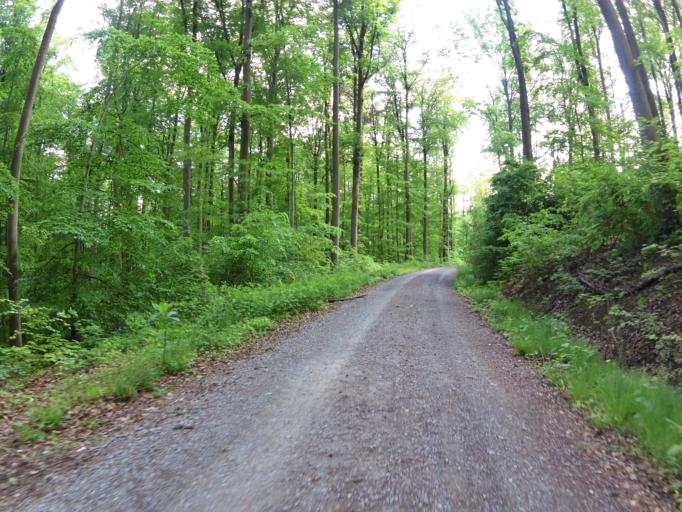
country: DE
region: Bavaria
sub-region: Regierungsbezirk Unterfranken
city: Wuerzburg
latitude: 49.7416
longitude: 9.8917
